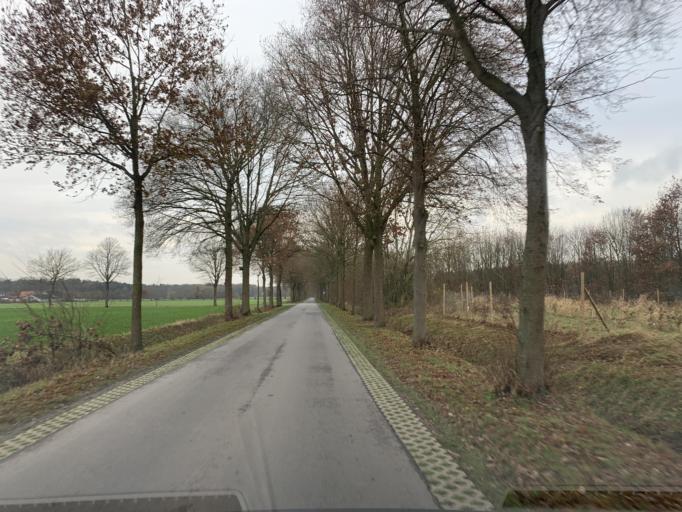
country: DE
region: North Rhine-Westphalia
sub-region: Regierungsbezirk Munster
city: Senden
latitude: 51.8898
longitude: 7.5443
